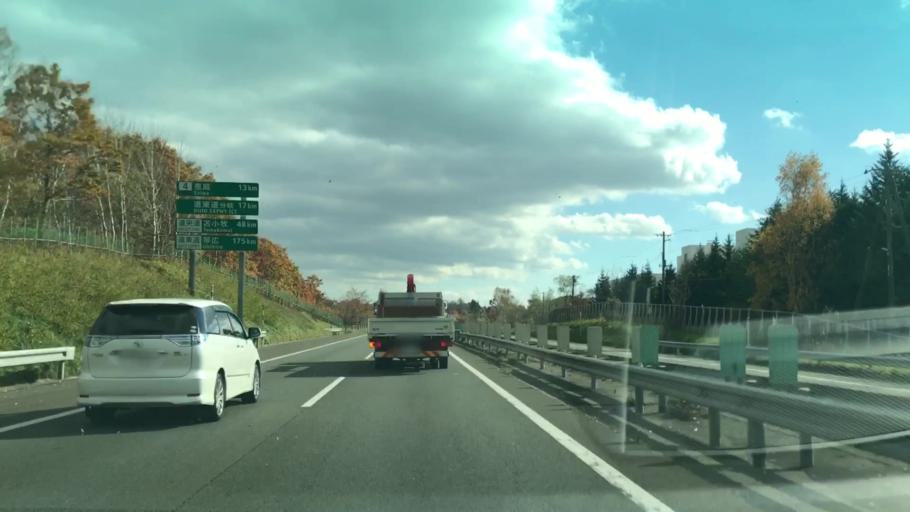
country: JP
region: Hokkaido
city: Kitahiroshima
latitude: 42.9719
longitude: 141.4852
